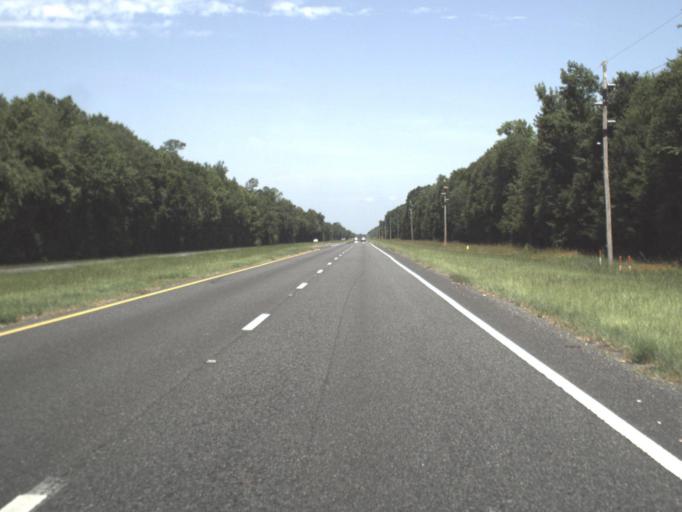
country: US
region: Florida
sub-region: Dixie County
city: Cross City
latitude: 29.6650
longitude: -83.2104
